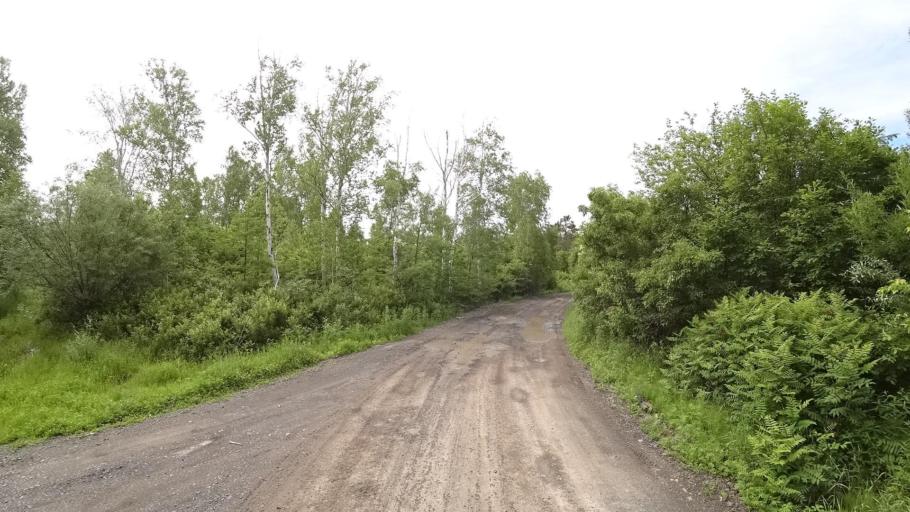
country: RU
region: Khabarovsk Krai
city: Amursk
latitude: 49.8998
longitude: 136.1502
